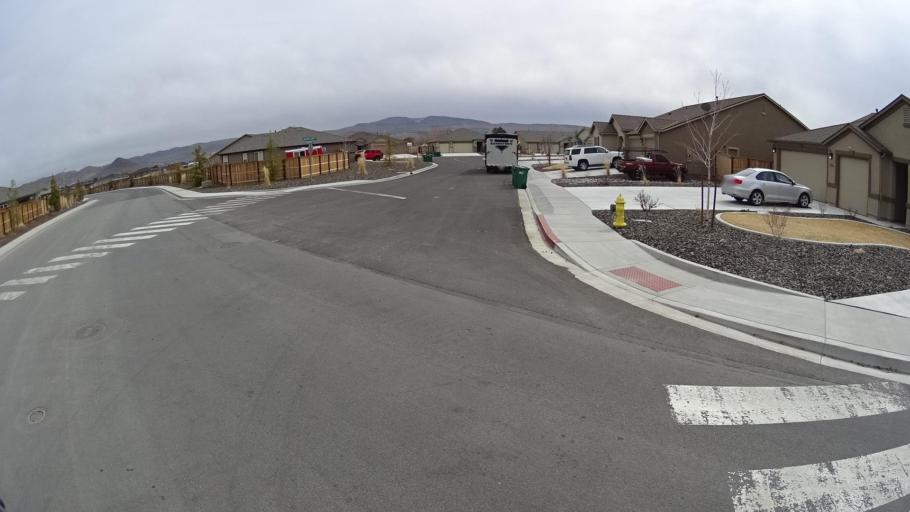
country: US
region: Nevada
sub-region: Washoe County
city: Spanish Springs
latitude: 39.6506
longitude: -119.7190
